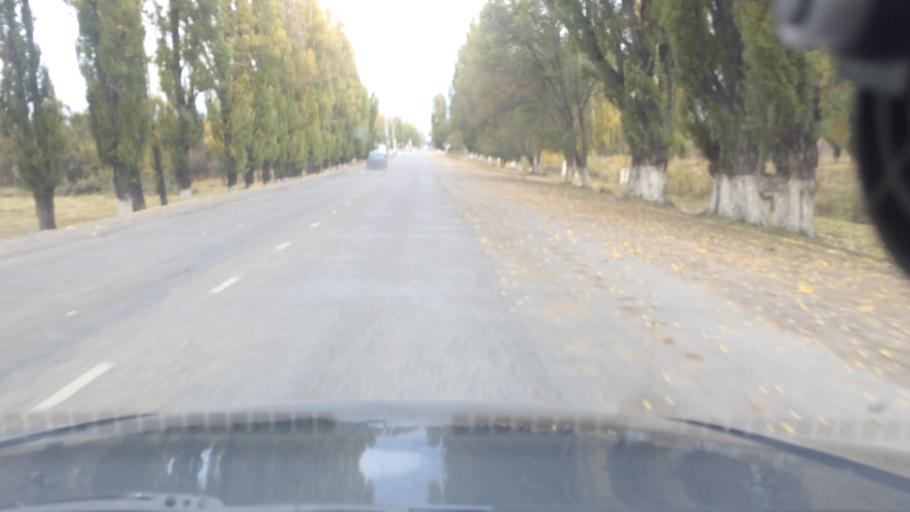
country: KG
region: Ysyk-Koel
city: Tyup
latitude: 42.7361
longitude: 78.3499
